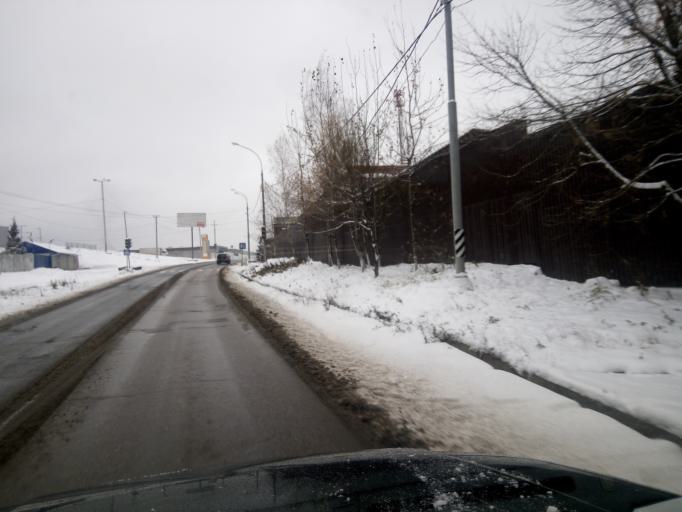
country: RU
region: Moskovskaya
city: Skhodnya
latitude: 55.9690
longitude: 37.3100
